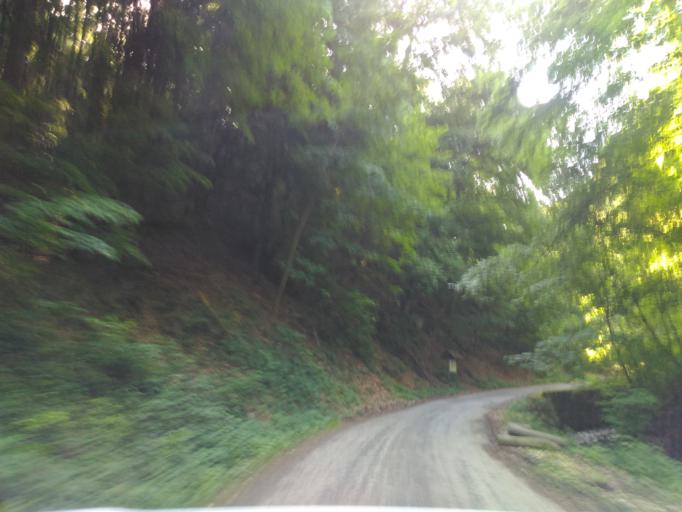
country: HU
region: Baranya
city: Hosszuheteny
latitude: 46.2246
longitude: 18.3305
